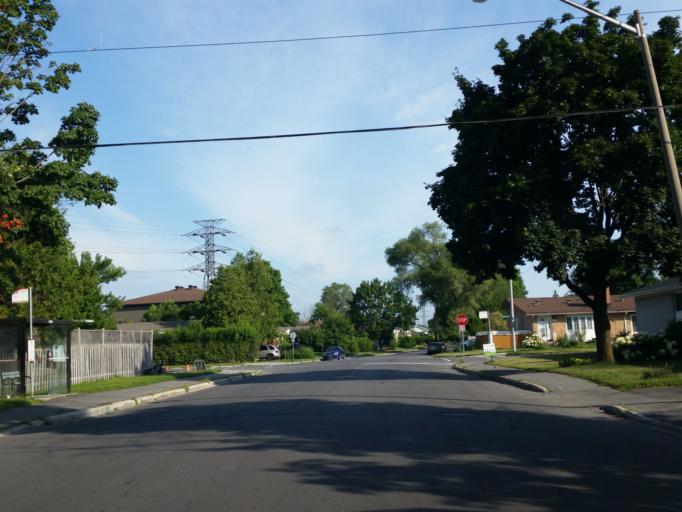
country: CA
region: Ontario
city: Ottawa
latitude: 45.3589
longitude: -75.7464
